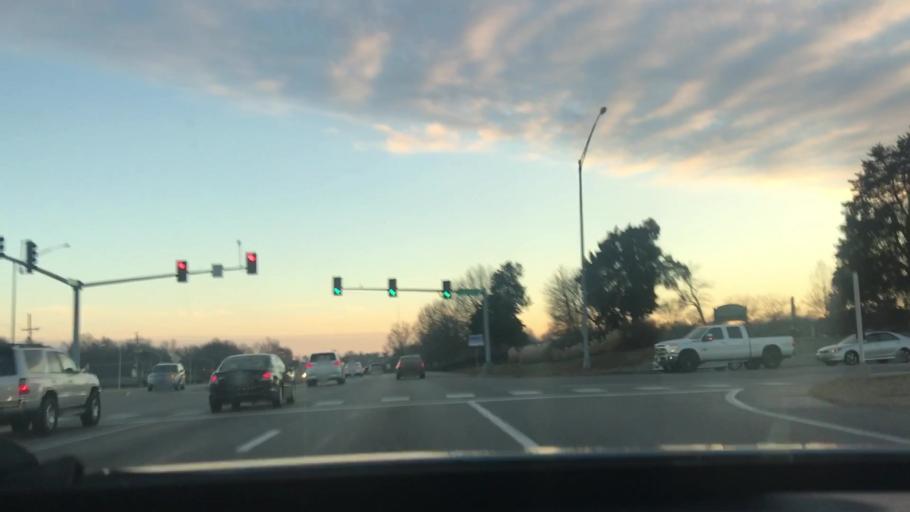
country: US
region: Missouri
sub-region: Jackson County
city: Lees Summit
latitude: 38.9179
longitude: -94.3620
